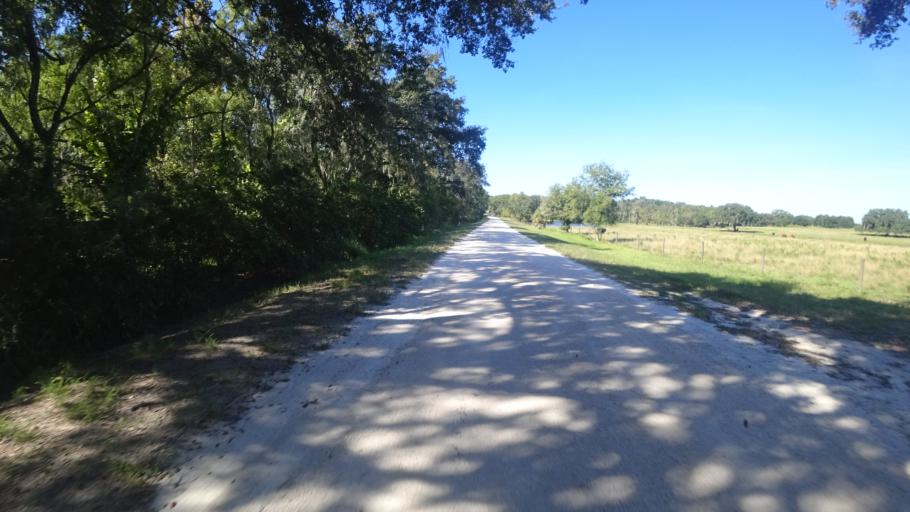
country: US
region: Florida
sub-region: Hillsborough County
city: Wimauma
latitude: 27.5965
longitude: -82.1914
